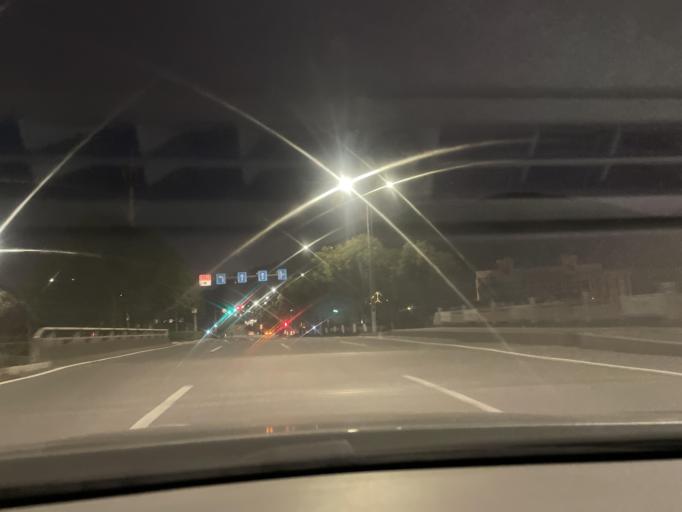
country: CN
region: Zhejiang Sheng
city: Wenzhou
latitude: 27.8840
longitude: 120.6725
